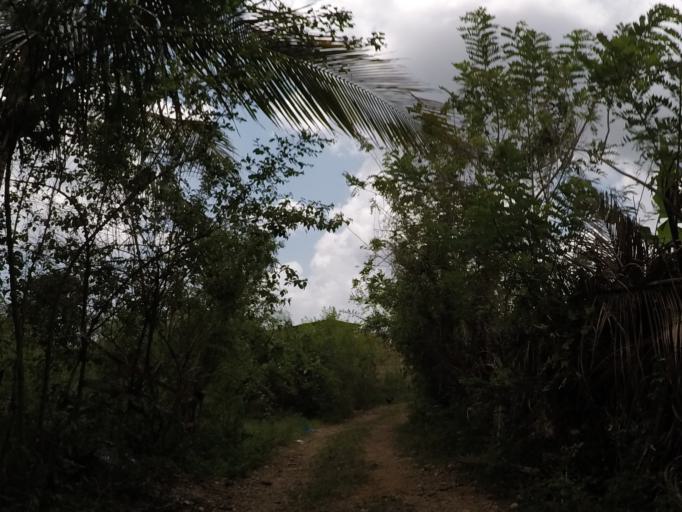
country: TZ
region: Zanzibar Central/South
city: Koani
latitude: -6.1728
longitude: 39.3098
